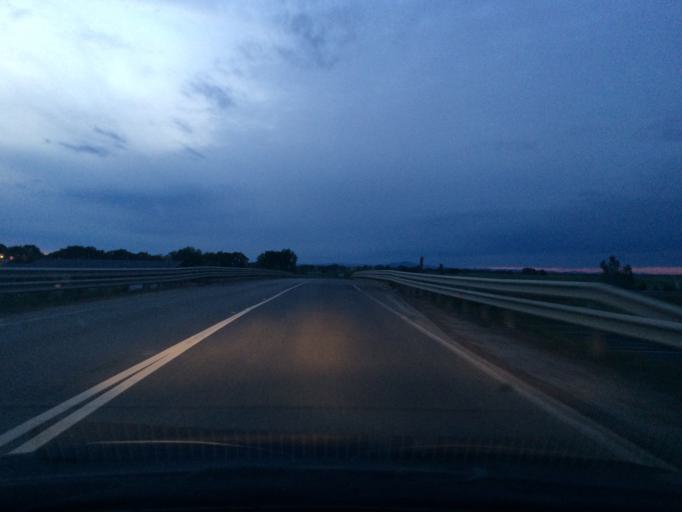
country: HU
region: Hajdu-Bihar
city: Hajdunanas
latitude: 47.8818
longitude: 21.4147
